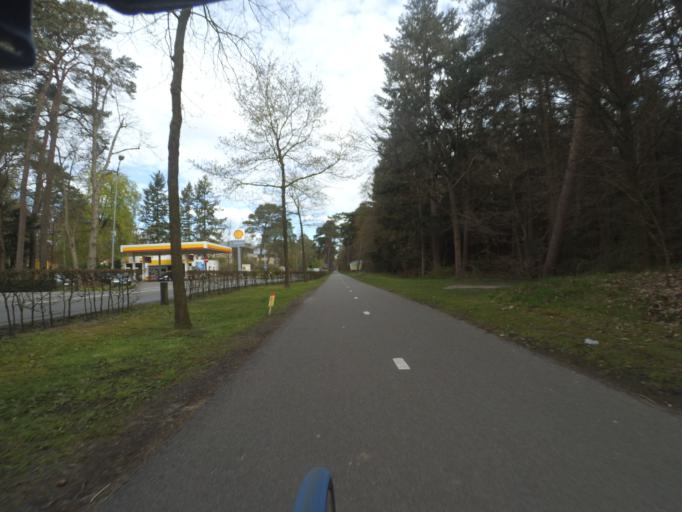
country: NL
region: Gelderland
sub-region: Gemeente Nunspeet
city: Nunspeet
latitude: 52.3652
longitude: 5.7849
